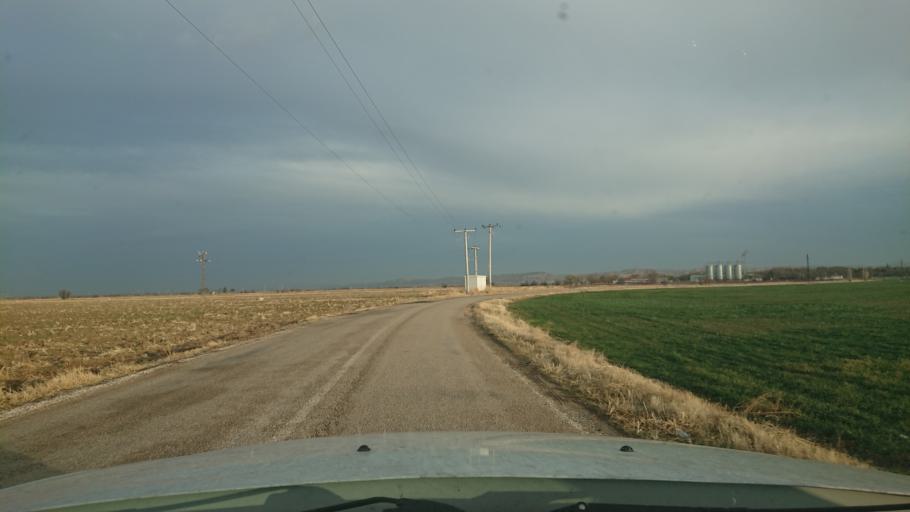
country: TR
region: Aksaray
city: Yesilova
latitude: 38.4496
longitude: 33.8346
